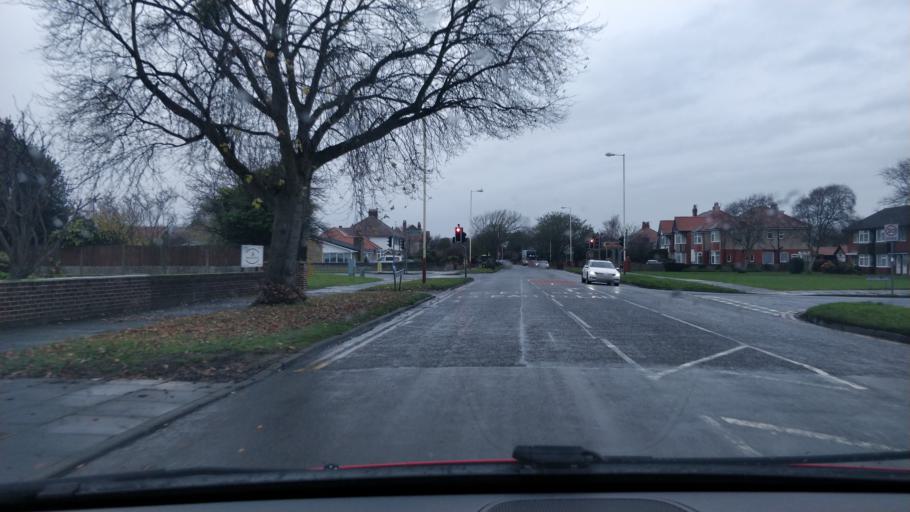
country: GB
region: England
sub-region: Sefton
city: Formby
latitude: 53.5964
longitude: -3.0369
